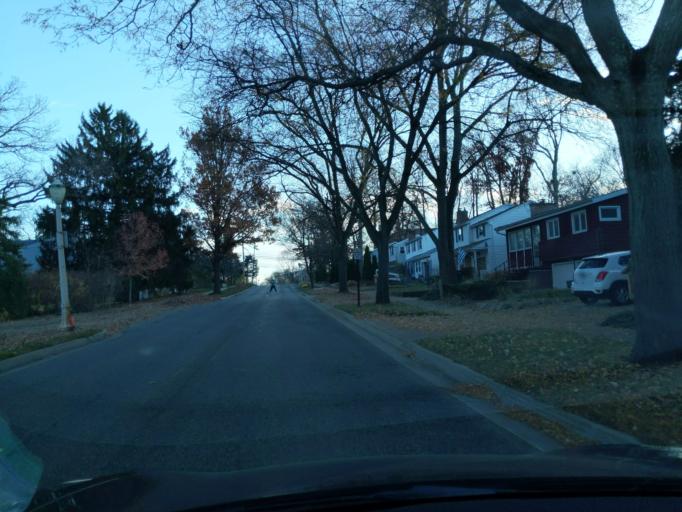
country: US
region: Michigan
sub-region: Ingham County
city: East Lansing
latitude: 42.7397
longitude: -84.4936
